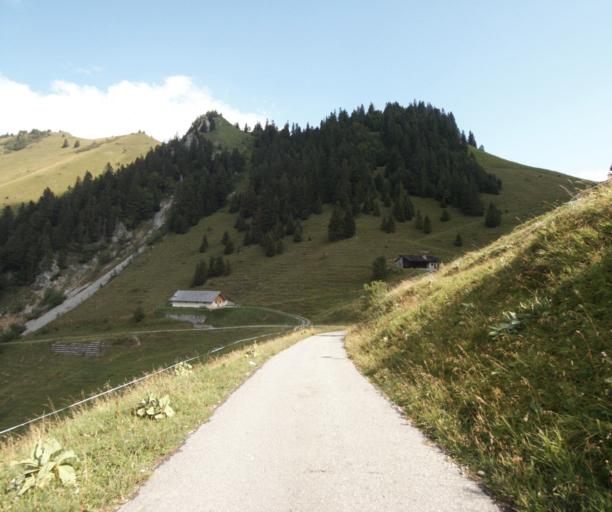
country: CH
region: Vaud
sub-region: Riviera-Pays-d'Enhaut District
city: Caux
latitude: 46.4201
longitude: 6.9947
